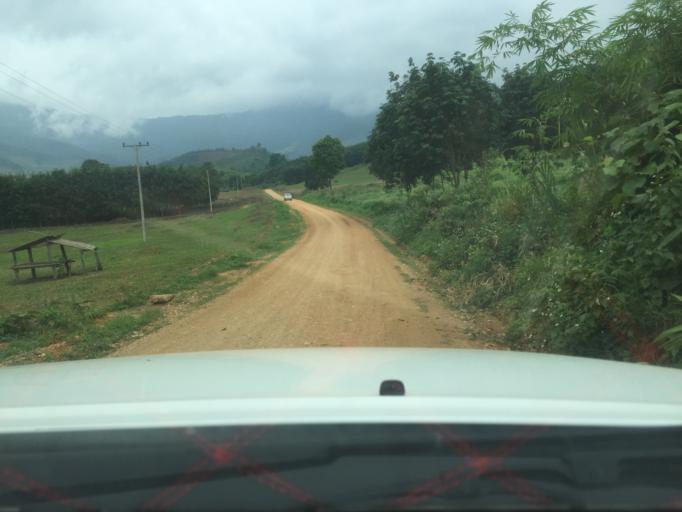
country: TH
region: Phayao
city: Phu Sang
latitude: 19.7412
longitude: 100.4602
